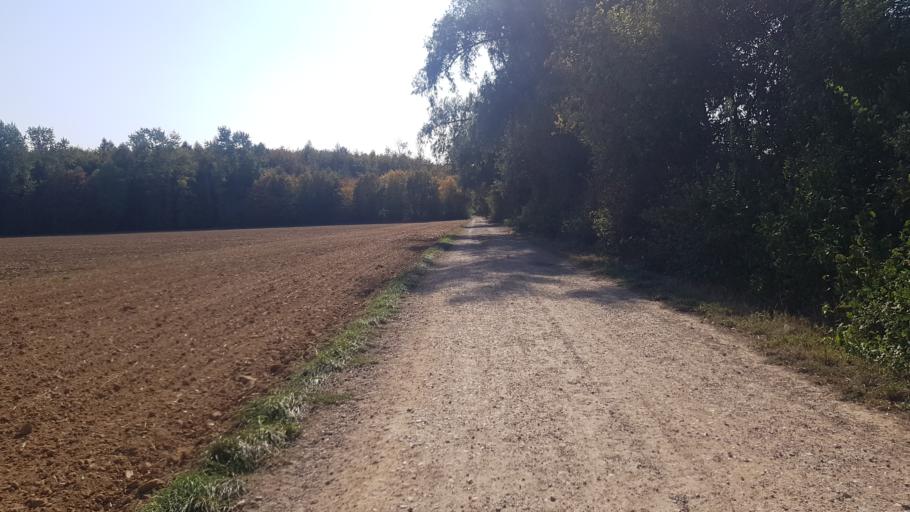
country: DE
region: North Rhine-Westphalia
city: Niedermerz
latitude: 50.8749
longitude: 6.2545
